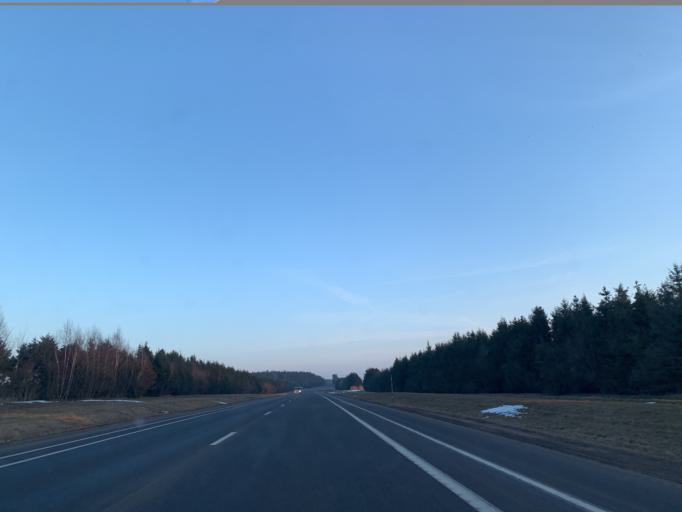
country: BY
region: Minsk
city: Haradzyeya
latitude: 53.2898
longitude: 26.5797
